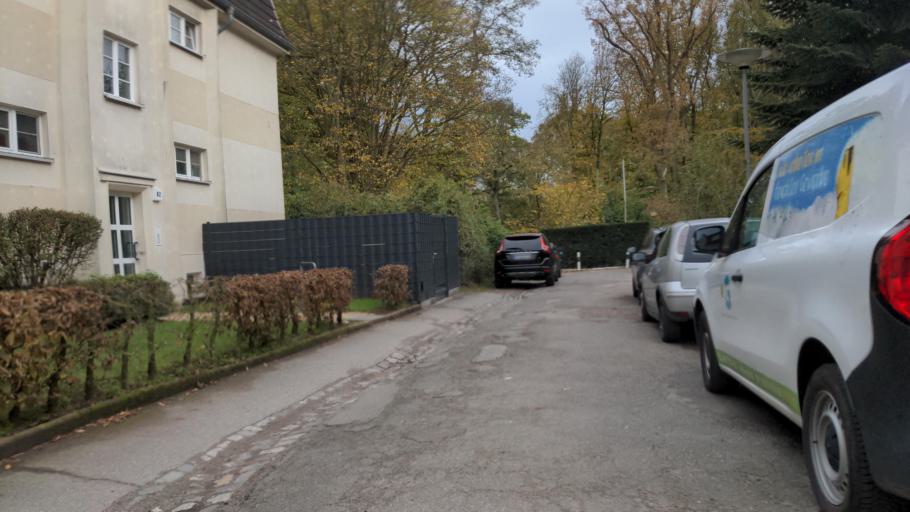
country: DE
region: Schleswig-Holstein
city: Luebeck
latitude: 53.8878
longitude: 10.7100
